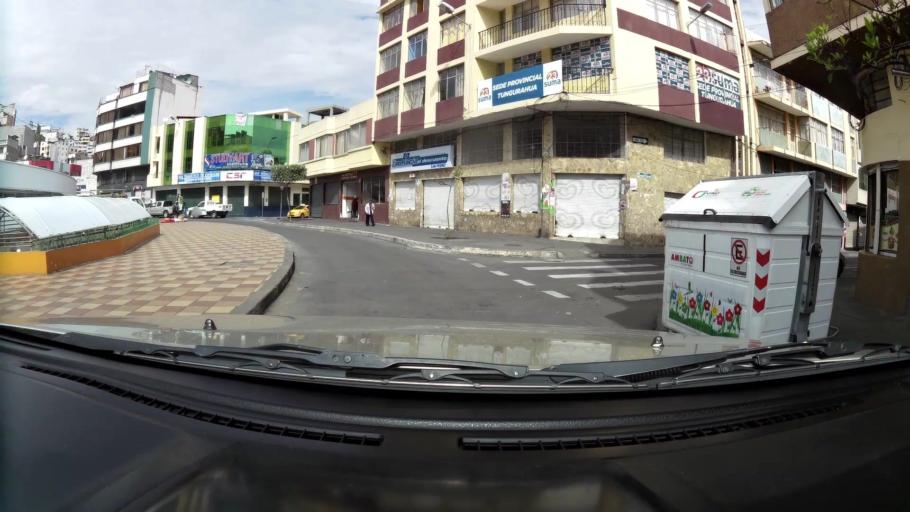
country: EC
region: Tungurahua
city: Ambato
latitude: -1.2441
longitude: -78.6266
